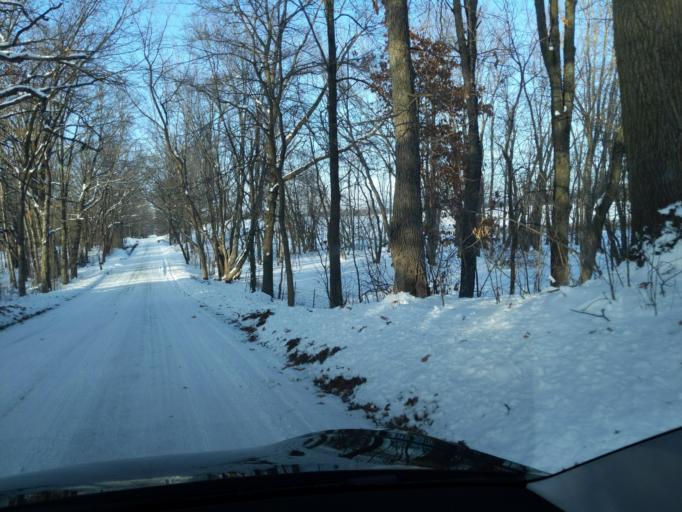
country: US
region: Michigan
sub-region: Ingham County
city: Stockbridge
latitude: 42.4517
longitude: -84.1038
